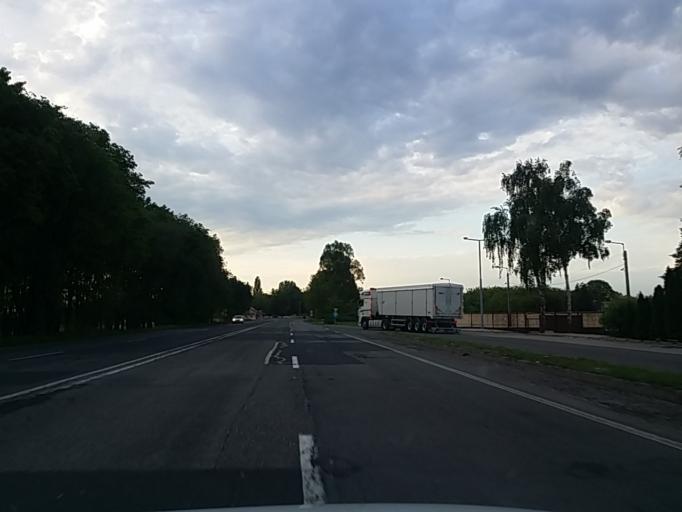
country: HU
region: Bacs-Kiskun
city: Kecskemet
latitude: 46.9683
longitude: 19.6367
